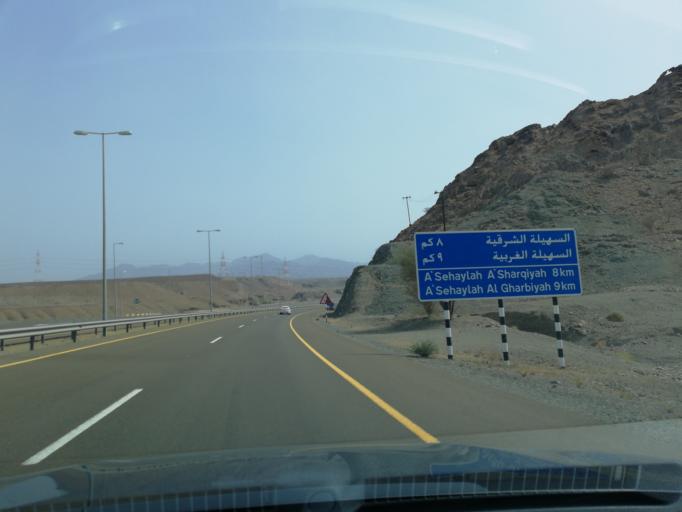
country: OM
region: Al Batinah
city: Al Liwa'
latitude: 24.2979
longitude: 56.4251
